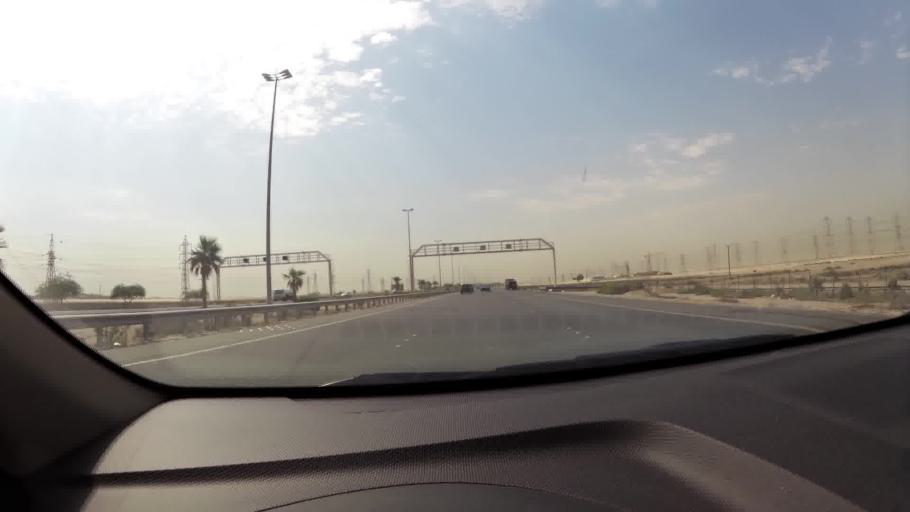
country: KW
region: Al Ahmadi
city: Al Fahahil
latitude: 28.8963
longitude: 48.2208
